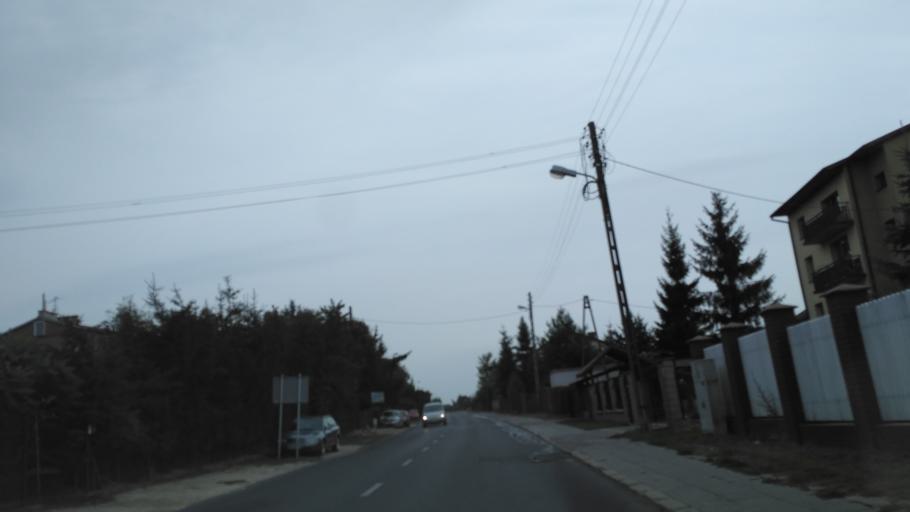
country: PL
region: Lublin Voivodeship
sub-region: Powiat lubelski
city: Lublin
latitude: 51.2191
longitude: 22.5891
